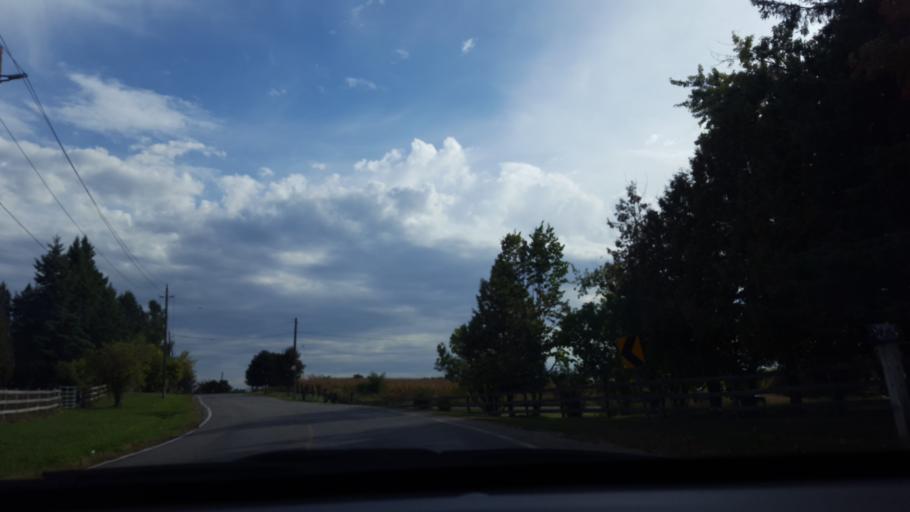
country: CA
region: Ontario
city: Vaughan
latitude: 43.8899
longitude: -79.6186
